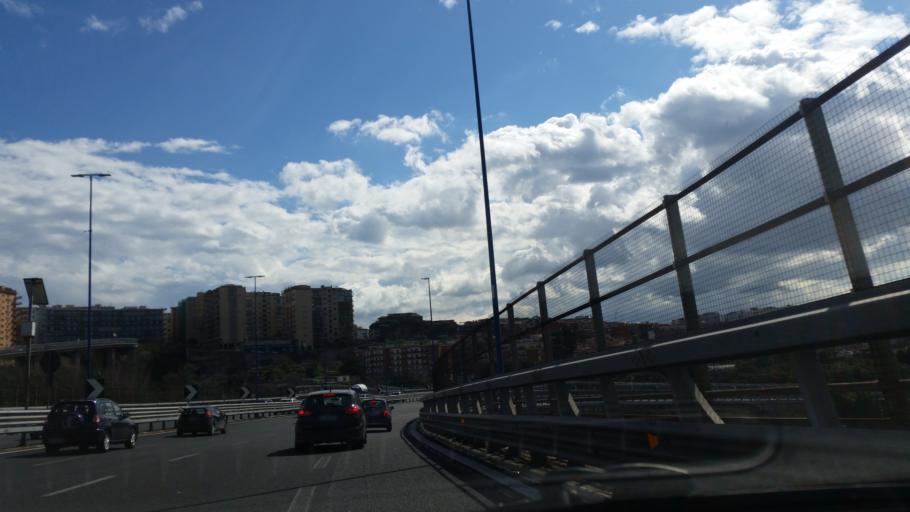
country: IT
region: Campania
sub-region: Provincia di Napoli
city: Napoli
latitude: 40.8463
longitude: 14.2161
